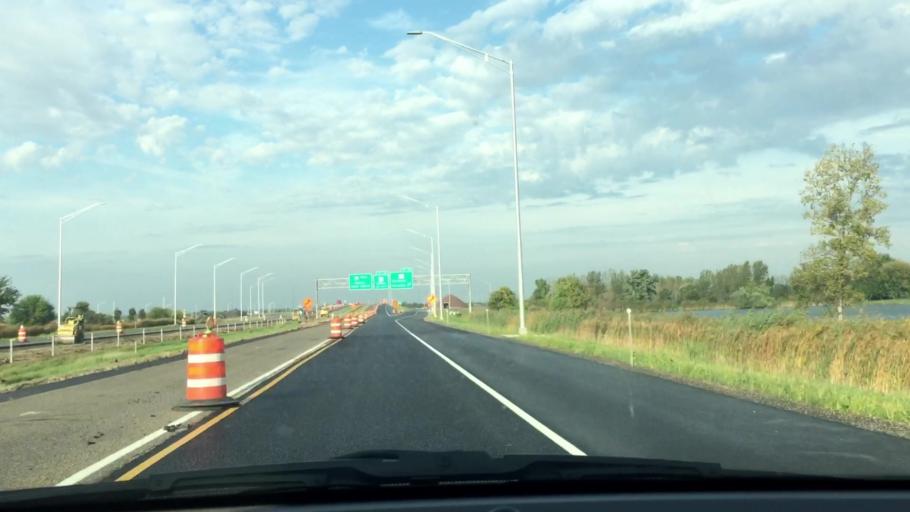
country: US
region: Illinois
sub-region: Ogle County
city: Rochelle
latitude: 41.9007
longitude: -89.0594
